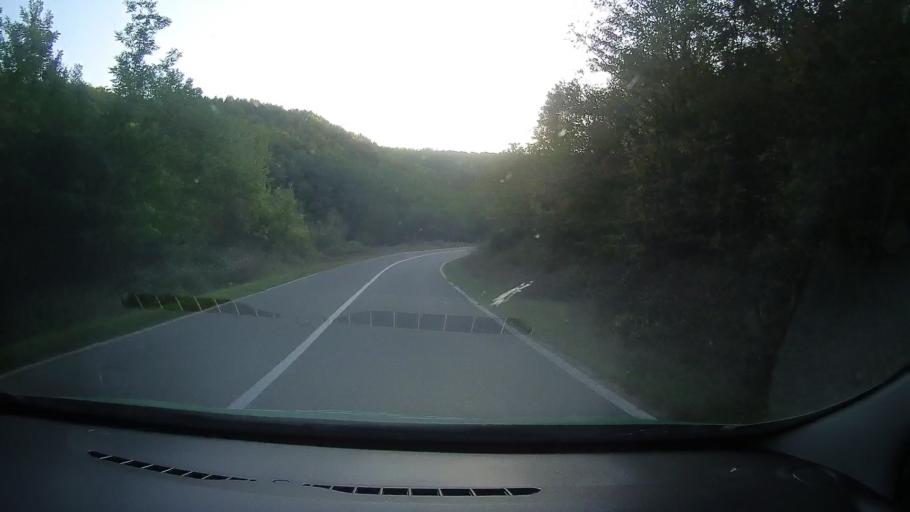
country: RO
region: Timis
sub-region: Comuna Traian Vuia
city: Traian Vuia
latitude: 45.7581
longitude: 22.1074
